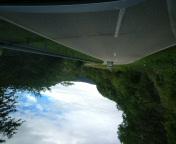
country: DE
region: Baden-Wuerttemberg
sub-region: Freiburg Region
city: Oppenau
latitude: 48.4398
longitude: 8.1713
